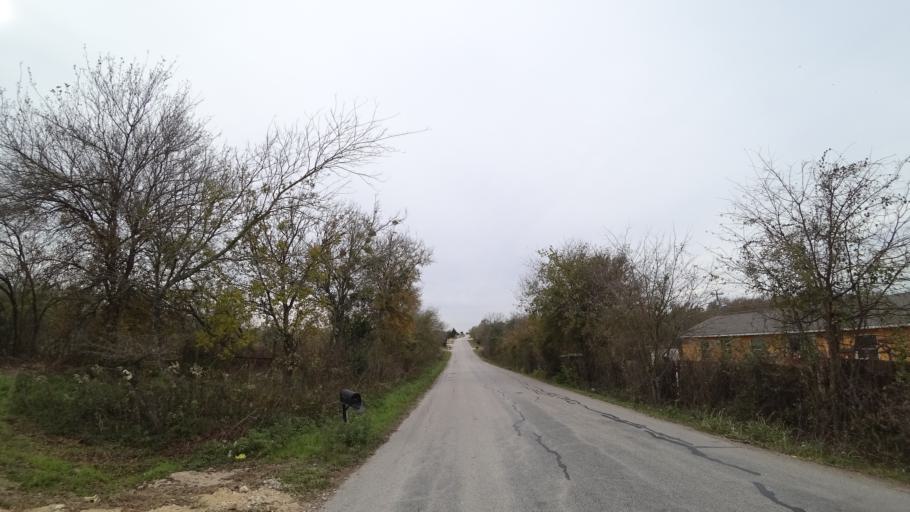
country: US
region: Texas
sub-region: Travis County
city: Garfield
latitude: 30.1090
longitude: -97.5863
